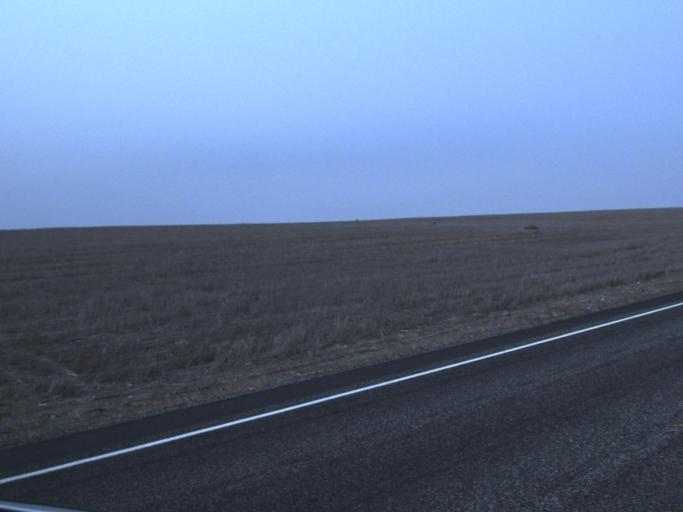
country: US
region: Washington
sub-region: Benton County
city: Prosser
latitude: 46.0886
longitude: -119.6020
